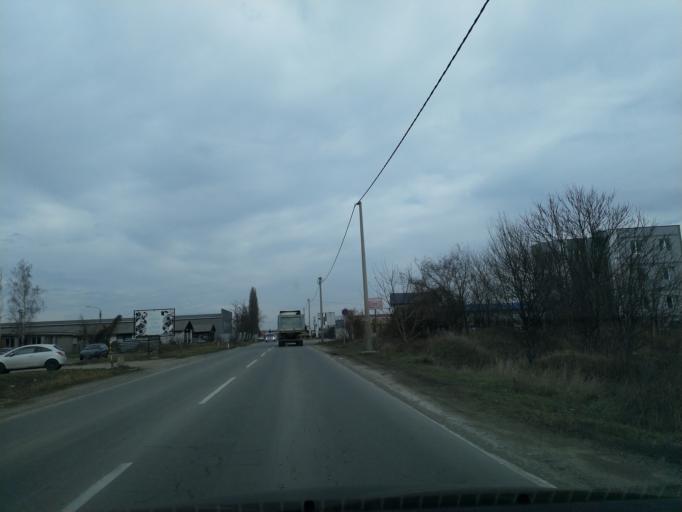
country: RS
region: Central Serbia
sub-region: Belgrade
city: Zvezdara
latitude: 44.7370
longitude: 20.5917
